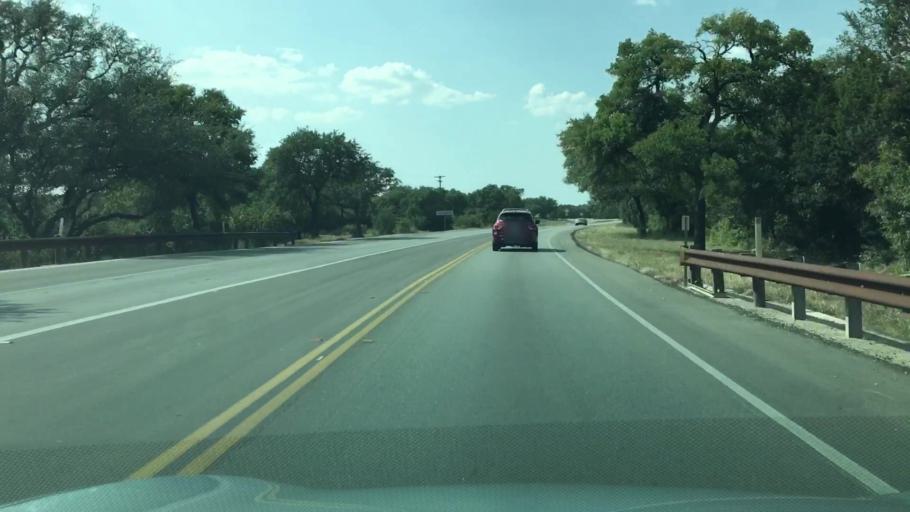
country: US
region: Texas
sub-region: Hays County
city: Wimberley
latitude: 29.9346
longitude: -98.0783
